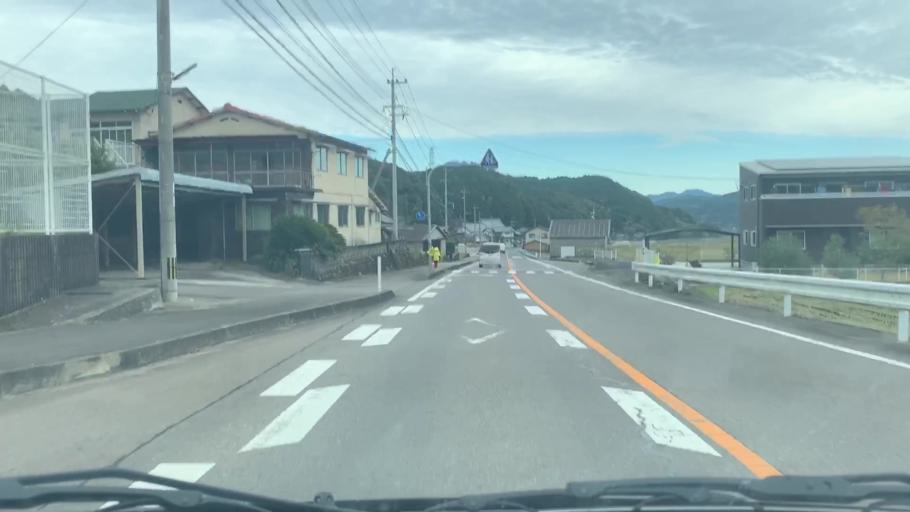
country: JP
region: Saga Prefecture
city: Takeocho-takeo
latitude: 33.1742
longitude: 129.9700
